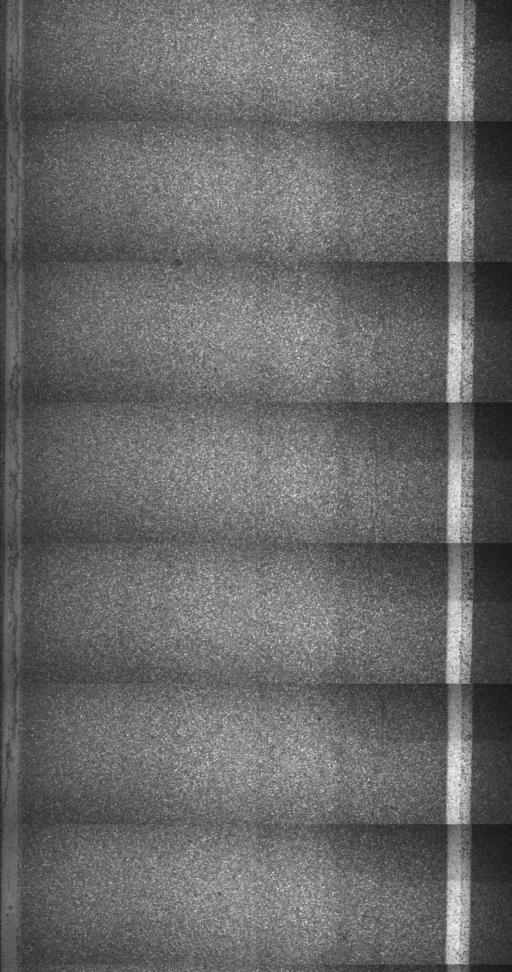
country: US
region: New Hampshire
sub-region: Grafton County
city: Woodsville
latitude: 44.1956
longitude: -72.1501
